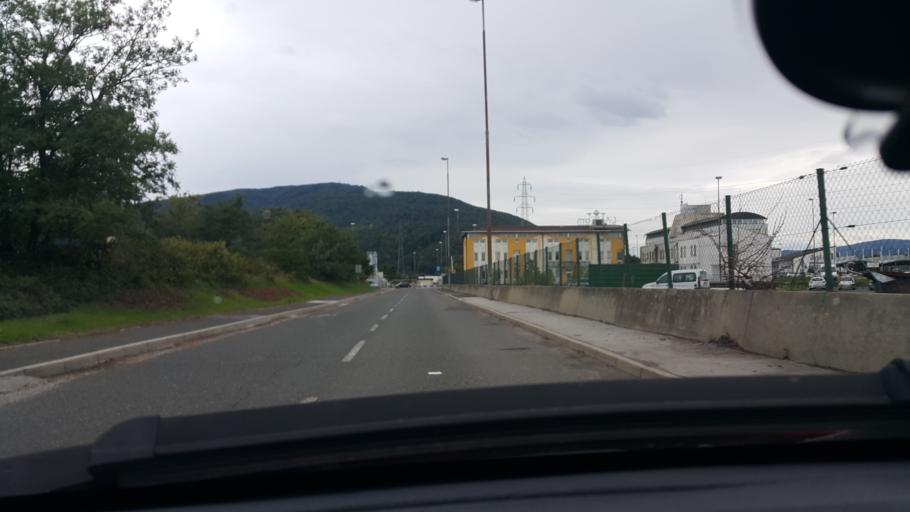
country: SI
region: Maribor
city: Razvanje
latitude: 46.5247
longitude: 15.6527
